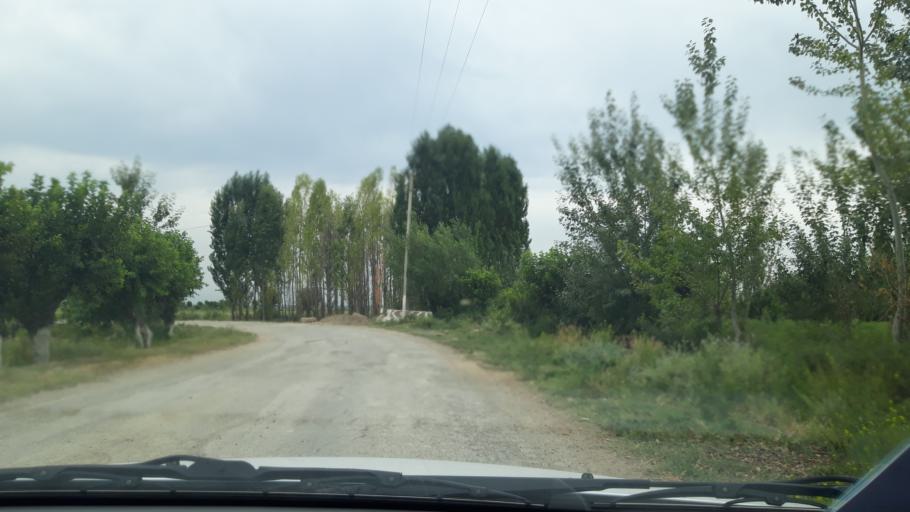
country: UZ
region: Namangan
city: Uychi
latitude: 41.0182
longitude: 71.9194
